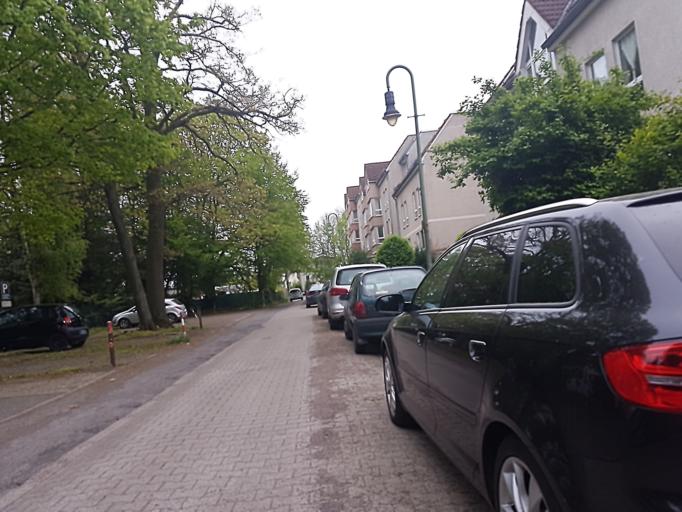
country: DE
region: Berlin
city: Waidmannslust
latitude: 52.6096
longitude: 13.3255
